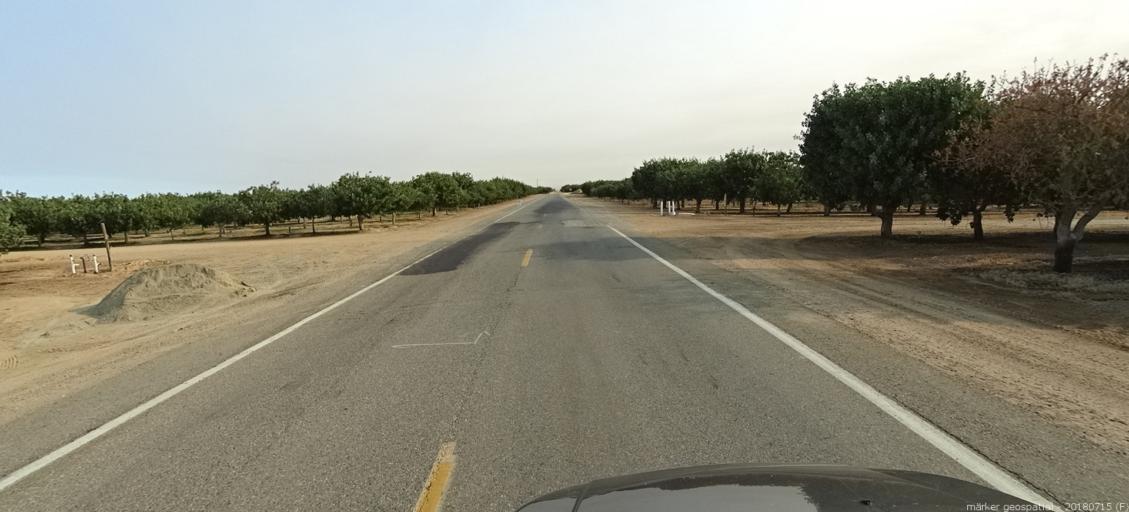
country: US
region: California
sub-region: Madera County
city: Madera Acres
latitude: 37.0505
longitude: -120.0564
